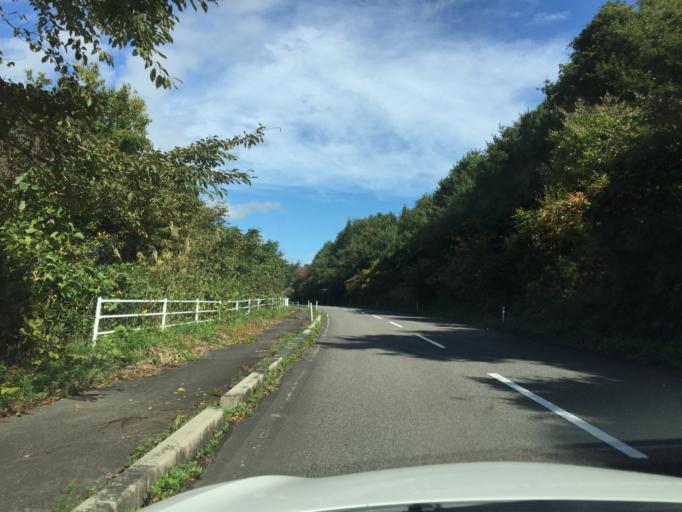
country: JP
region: Fukushima
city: Miharu
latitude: 37.4344
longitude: 140.5252
